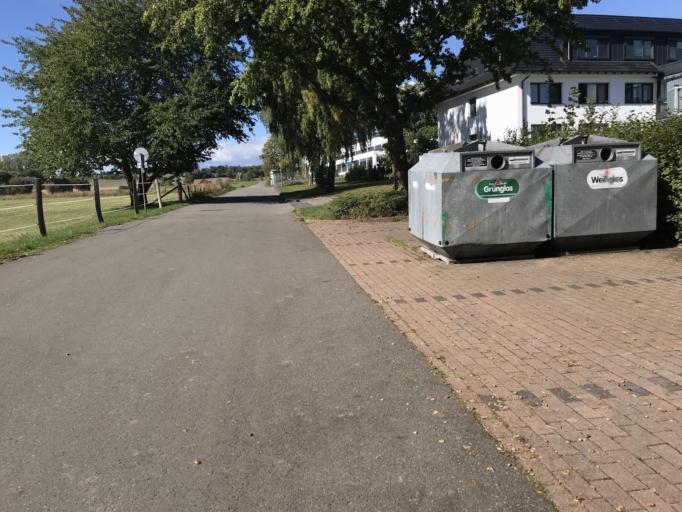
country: DE
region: Hesse
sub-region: Regierungsbezirk Kassel
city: Vohl
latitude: 51.2579
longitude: 8.9354
